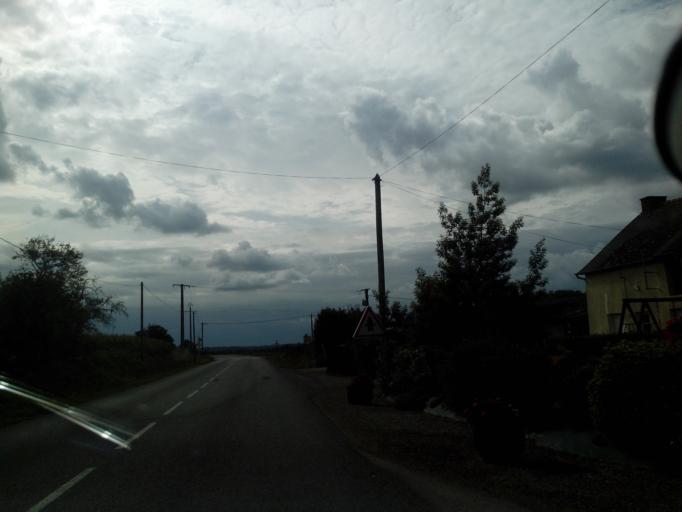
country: FR
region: Brittany
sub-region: Departement du Morbihan
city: Mauron
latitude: 48.1186
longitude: -2.2886
